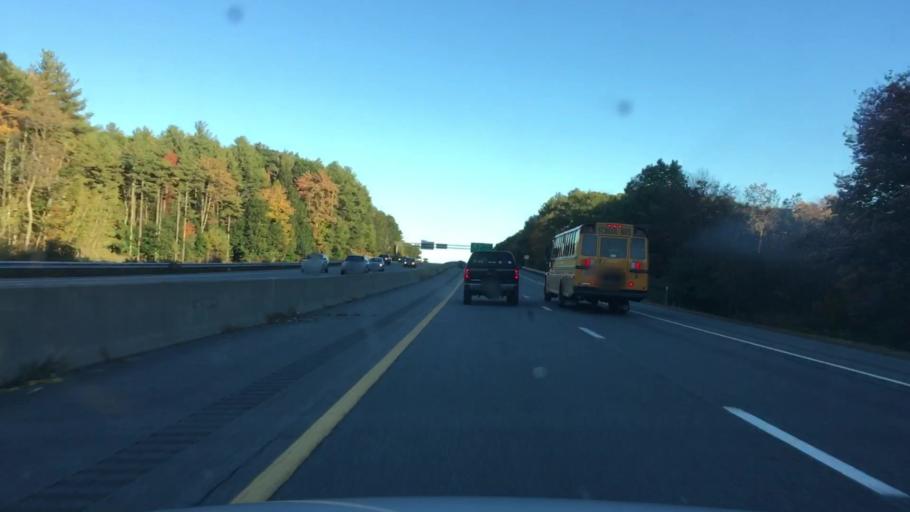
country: US
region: New Hampshire
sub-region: Rockingham County
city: Hampton
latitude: 42.9642
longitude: -70.8758
